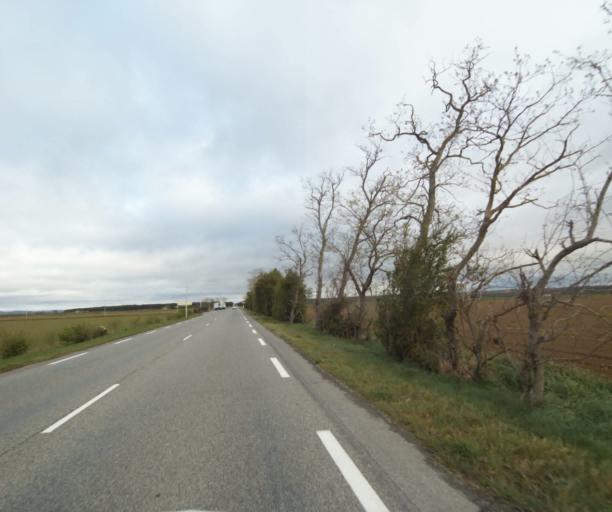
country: FR
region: Midi-Pyrenees
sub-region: Departement de l'Ariege
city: Saverdun
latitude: 43.2622
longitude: 1.5581
